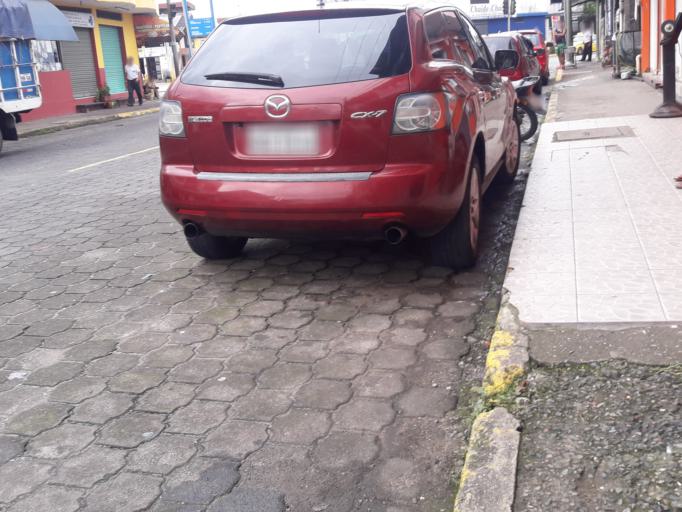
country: EC
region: Napo
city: Tena
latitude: -0.9983
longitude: -77.8134
